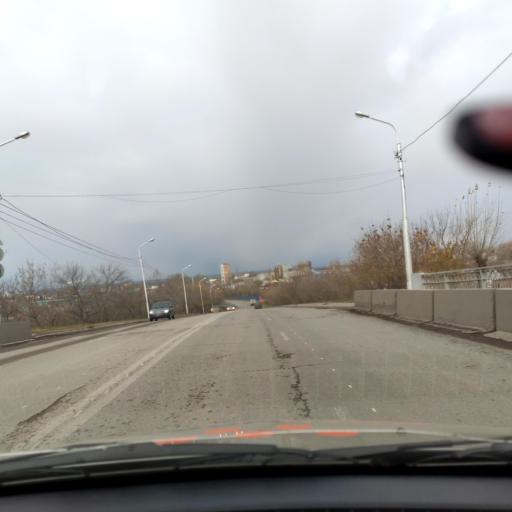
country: RU
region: Bashkortostan
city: Ufa
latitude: 54.7416
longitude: 55.9302
